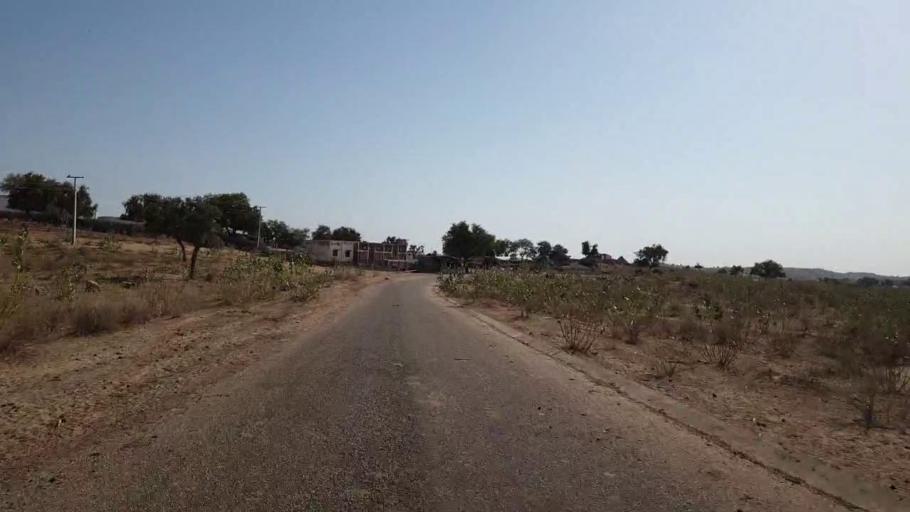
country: PK
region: Sindh
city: Umarkot
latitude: 25.1155
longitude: 70.0422
